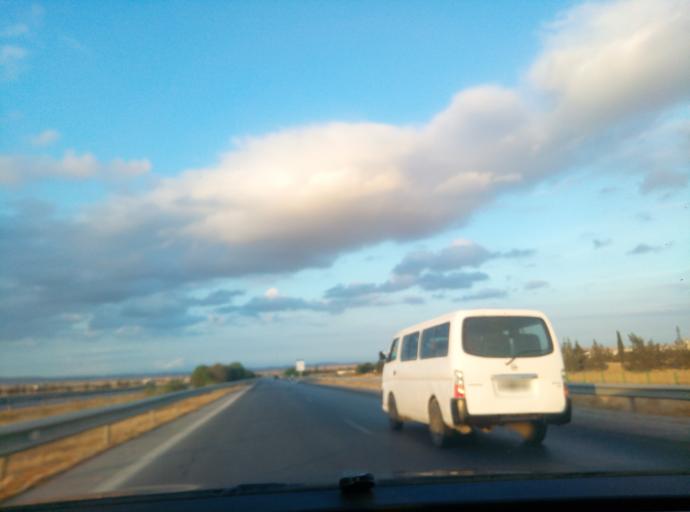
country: TN
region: Manouba
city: El Battan
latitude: 36.6874
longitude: 9.9220
